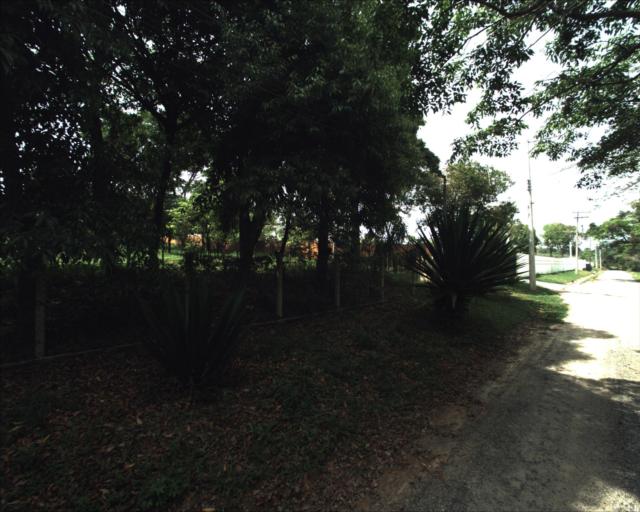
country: BR
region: Sao Paulo
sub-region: Salto De Pirapora
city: Salto de Pirapora
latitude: -23.5649
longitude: -47.5372
